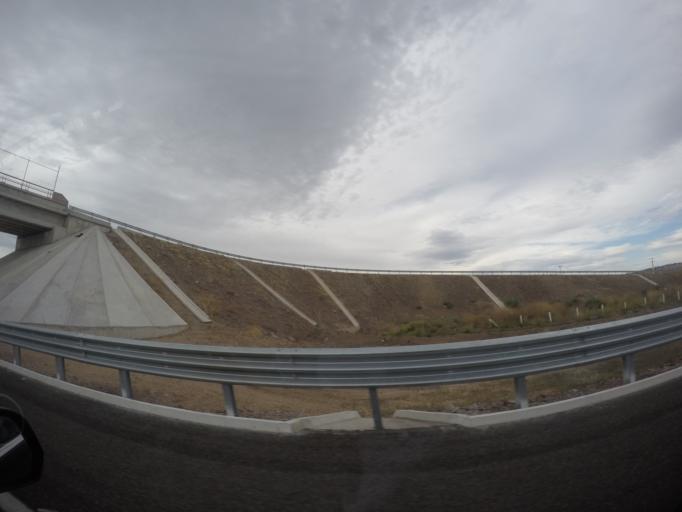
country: MX
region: Guanajuato
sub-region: Irapuato
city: Serrano
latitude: 20.7765
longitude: -101.4050
